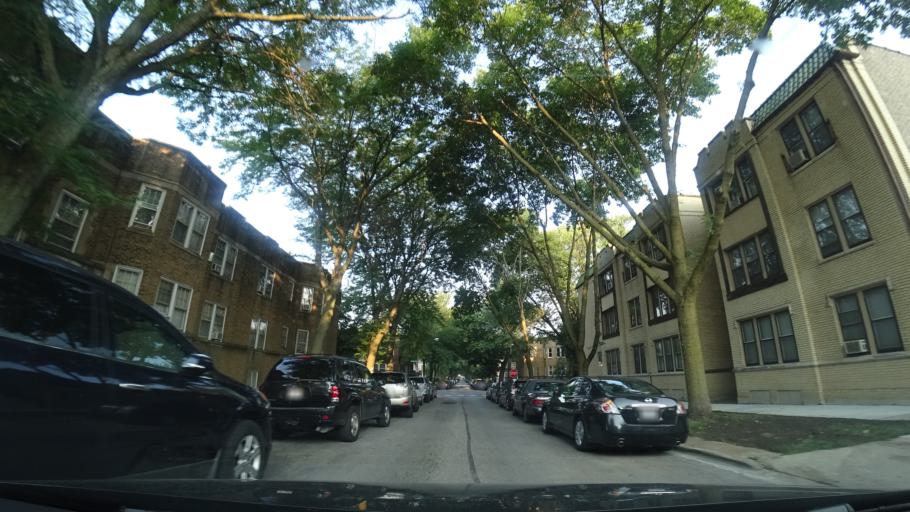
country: US
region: Illinois
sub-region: Cook County
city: Lincolnwood
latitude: 41.9850
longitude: -87.6913
